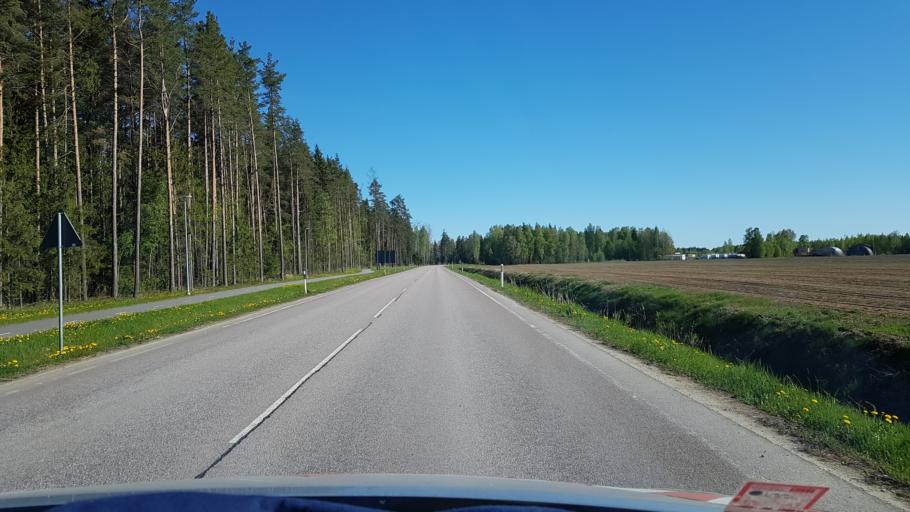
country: EE
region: Polvamaa
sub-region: Polva linn
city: Polva
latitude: 58.0919
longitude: 27.0930
